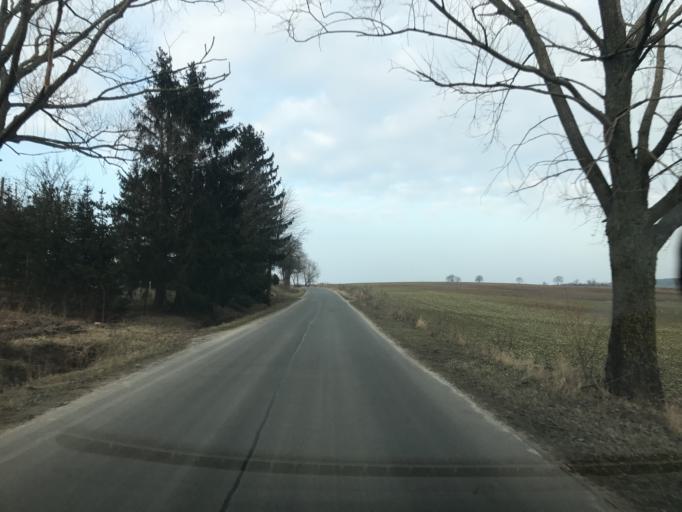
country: PL
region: Kujawsko-Pomorskie
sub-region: Powiat golubsko-dobrzynski
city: Kowalewo Pomorskie
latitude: 53.1772
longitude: 18.9611
